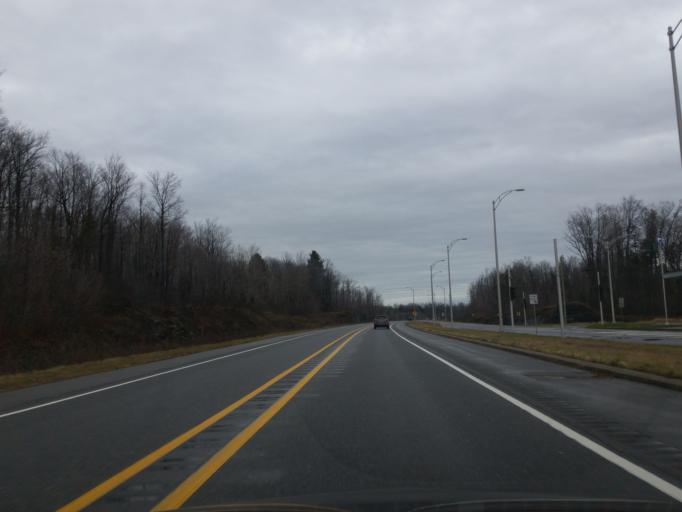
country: CA
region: Ontario
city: Clarence-Rockland
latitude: 45.6255
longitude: -75.3482
